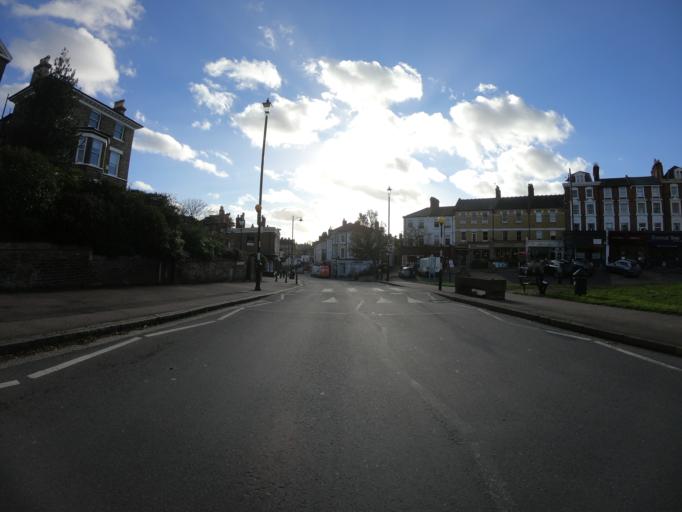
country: GB
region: England
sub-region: Greater London
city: Blackheath
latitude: 51.4676
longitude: 0.0088
